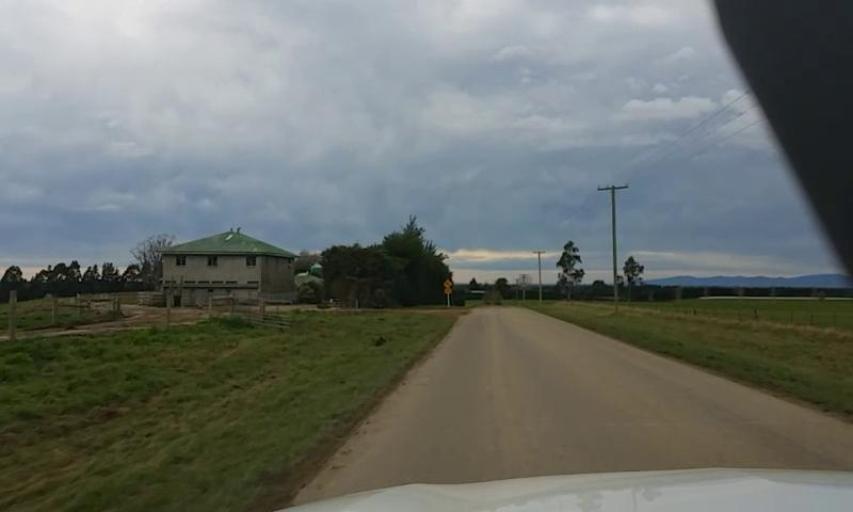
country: NZ
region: Canterbury
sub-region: Waimakariri District
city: Kaiapoi
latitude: -43.2988
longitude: 172.4809
